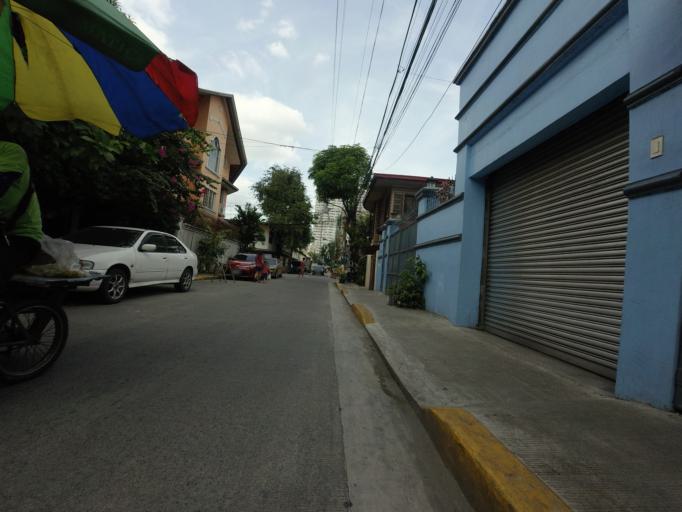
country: PH
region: Metro Manila
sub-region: City of Manila
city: Quiapo
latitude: 14.5806
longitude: 120.9958
